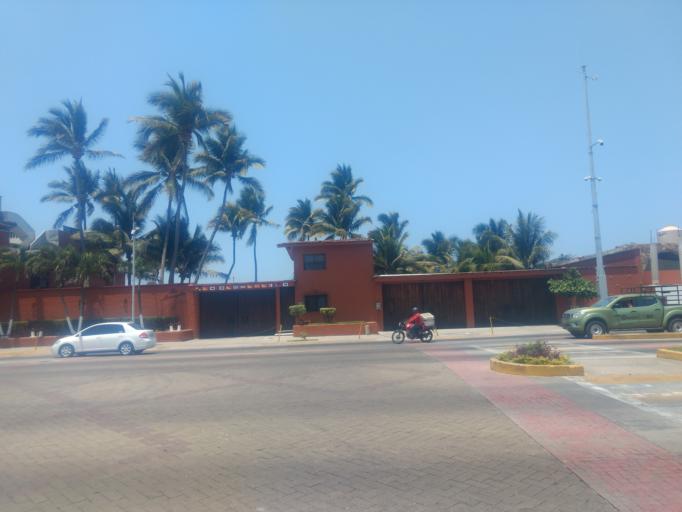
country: MX
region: Colima
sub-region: Manzanillo
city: Manzanillo
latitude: 19.0952
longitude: -104.3191
